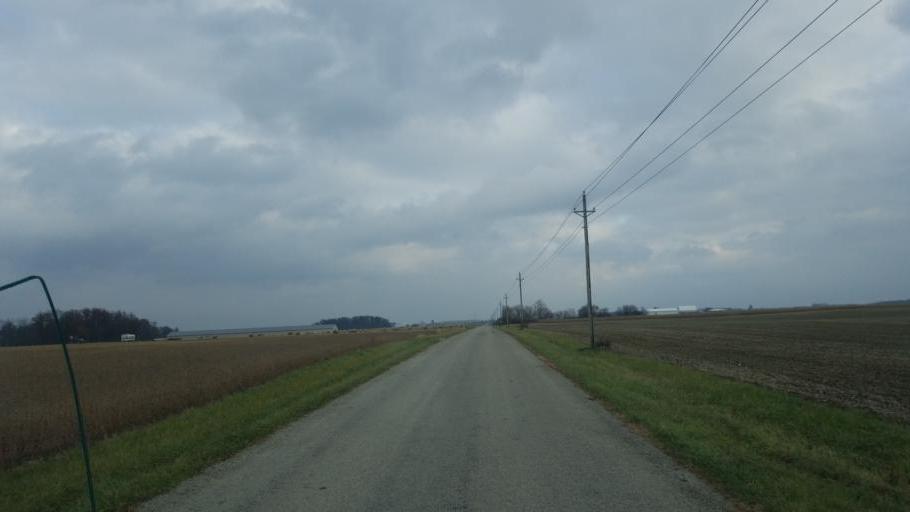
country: US
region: Indiana
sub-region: Adams County
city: Geneva
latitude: 40.5132
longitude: -84.8759
